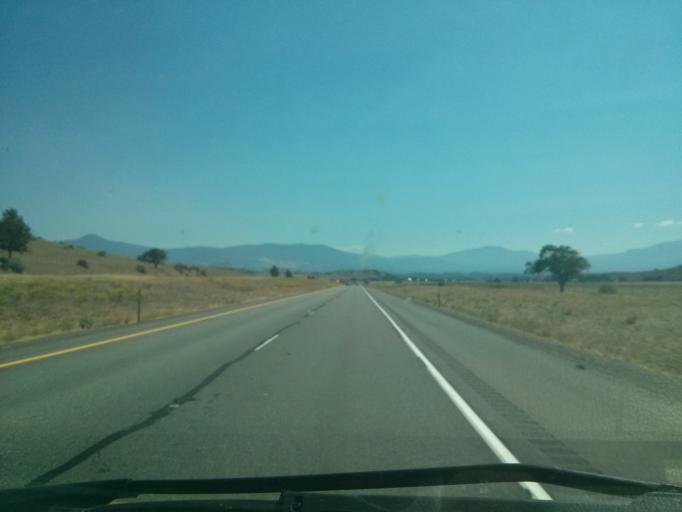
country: US
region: California
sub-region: Siskiyou County
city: Montague
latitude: 41.6603
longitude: -122.5772
